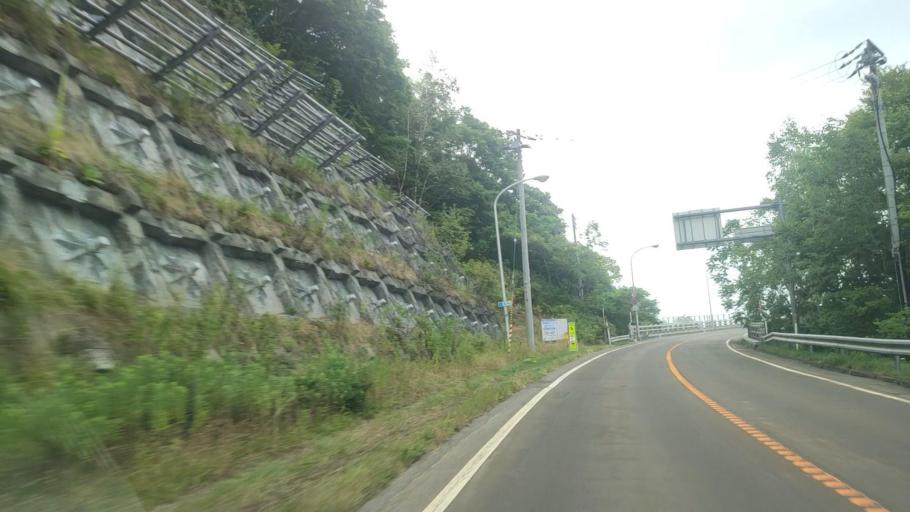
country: JP
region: Hokkaido
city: Otaru
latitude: 43.1360
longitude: 141.0389
